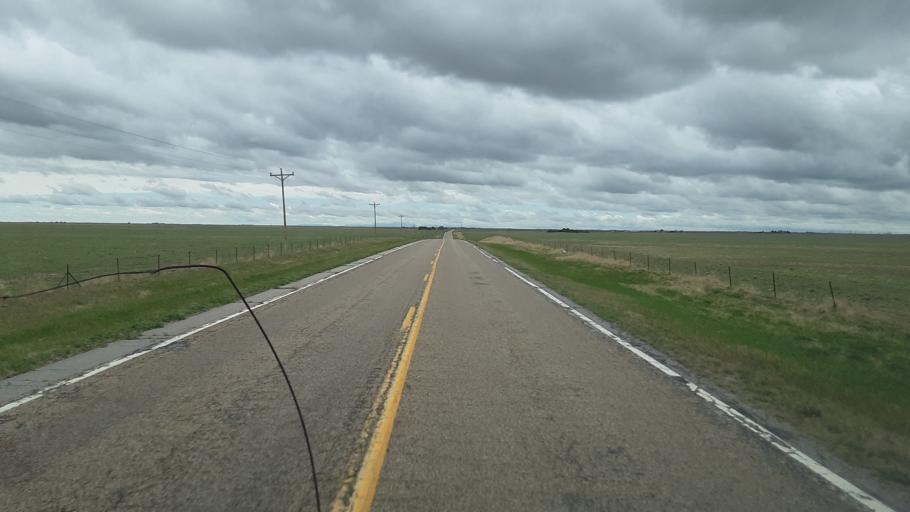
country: US
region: Colorado
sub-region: El Paso County
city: Ellicott
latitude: 38.8398
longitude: -103.9472
